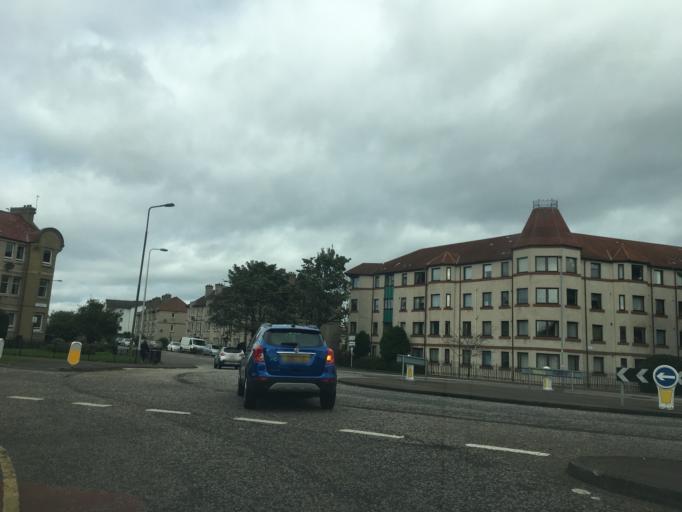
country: GB
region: Scotland
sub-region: West Lothian
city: Seafield
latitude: 55.9619
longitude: -3.1532
